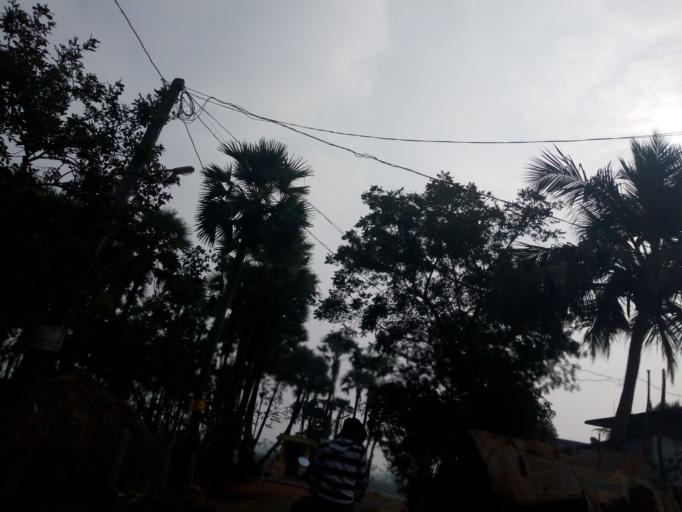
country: IN
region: Andhra Pradesh
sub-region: West Godavari
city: Tadepallegudem
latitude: 16.8469
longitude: 81.3373
